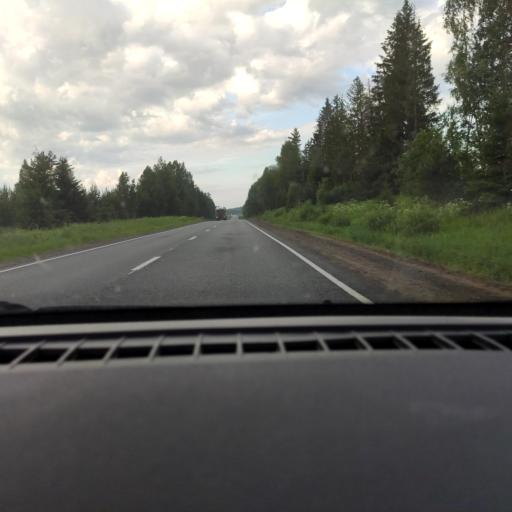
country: RU
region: Udmurtiya
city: Votkinsk
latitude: 57.2051
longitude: 54.1619
